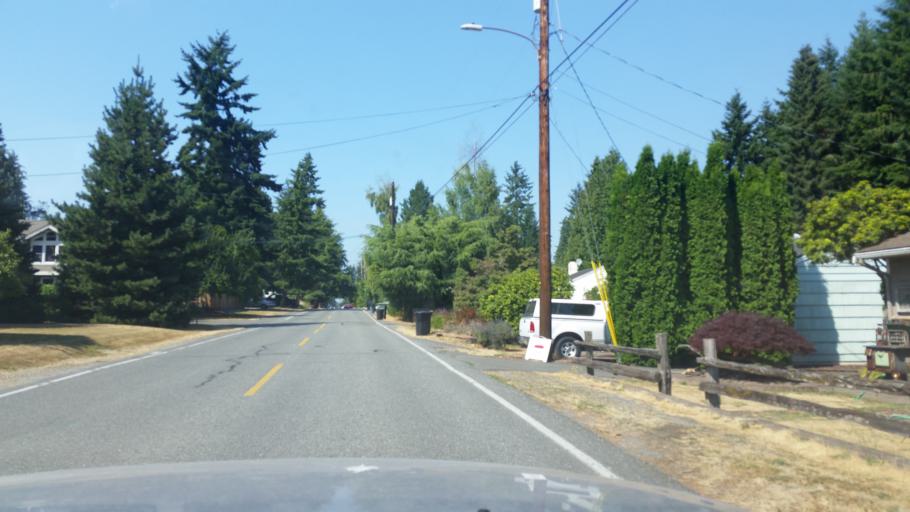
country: US
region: Washington
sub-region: Snohomish County
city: Esperance
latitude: 47.8000
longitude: -122.3410
